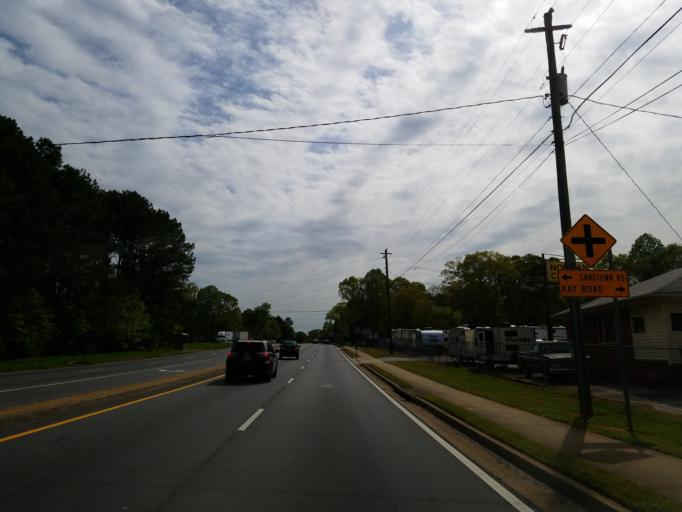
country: US
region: Georgia
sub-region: Cobb County
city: Fair Oaks
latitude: 33.9119
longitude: -84.5572
